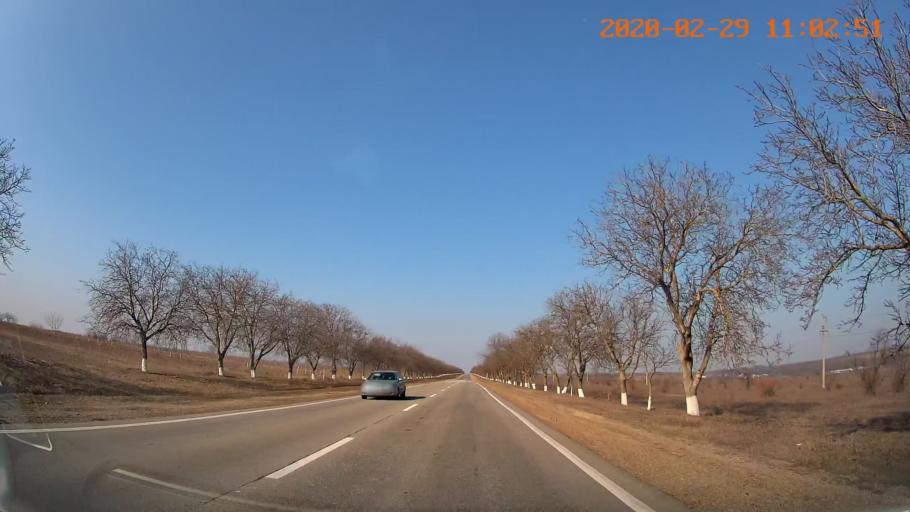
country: MD
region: Telenesti
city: Grigoriopol
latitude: 47.1753
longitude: 29.2300
